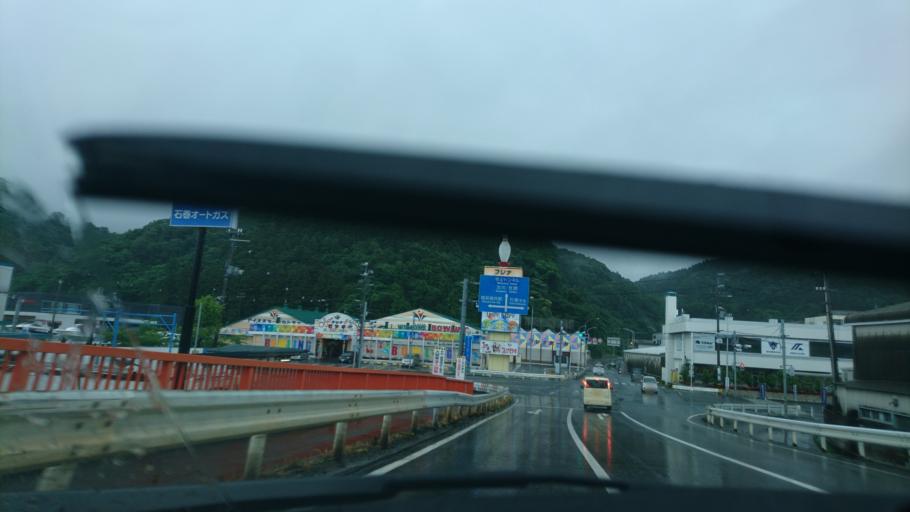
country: JP
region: Miyagi
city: Ishinomaki
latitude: 38.4369
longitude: 141.3181
